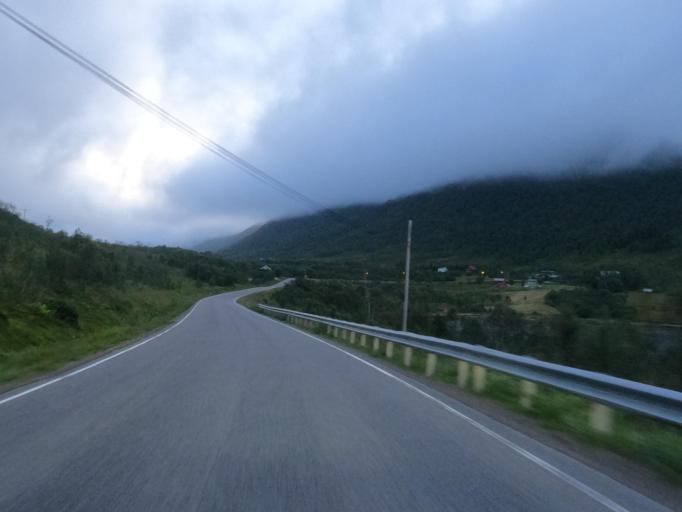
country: NO
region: Nordland
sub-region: Lodingen
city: Lodingen
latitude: 68.6136
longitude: 15.7716
